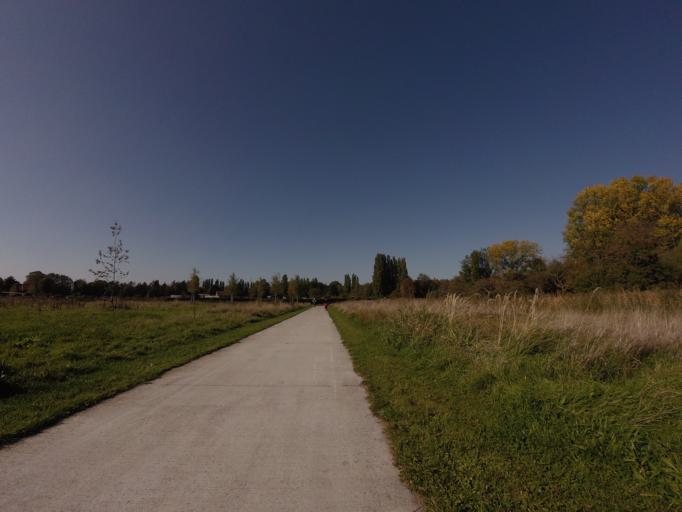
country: BE
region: Flanders
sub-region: Provincie Antwerpen
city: Borsbeek
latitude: 51.2082
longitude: 4.4847
